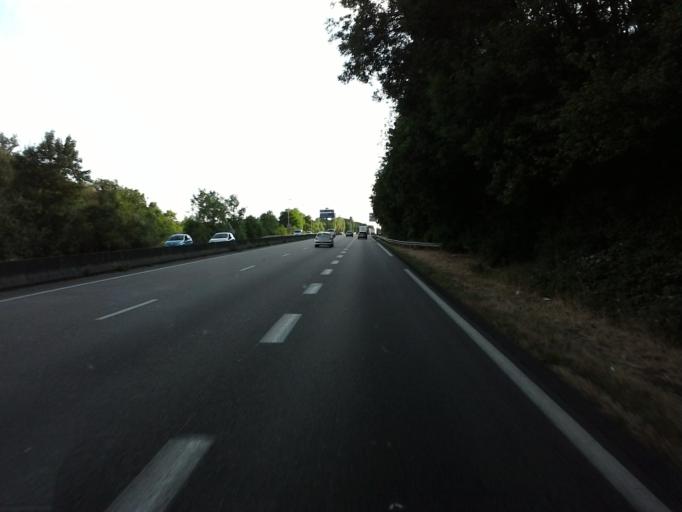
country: FR
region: Lorraine
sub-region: Departement de Meurthe-et-Moselle
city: Laxou
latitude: 48.7087
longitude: 6.1427
